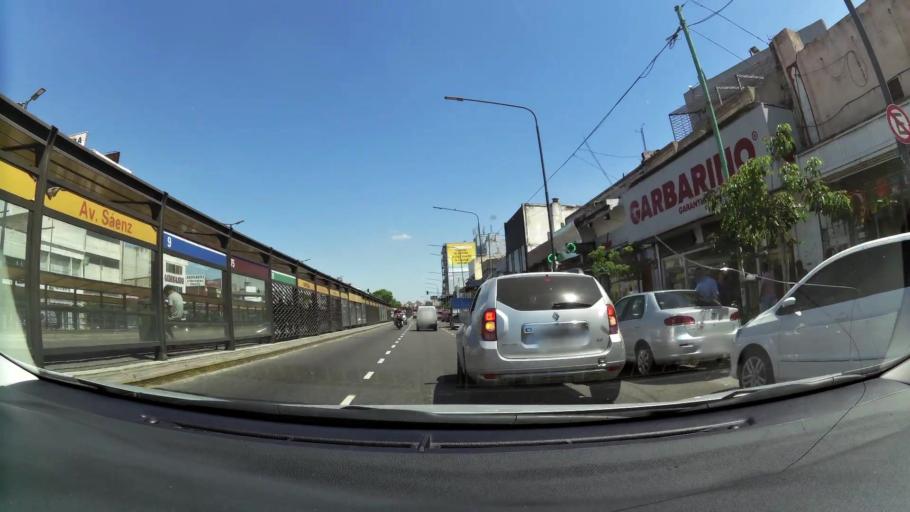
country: AR
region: Buenos Aires
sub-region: Partido de Avellaneda
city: Avellaneda
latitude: -34.6525
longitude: -58.4165
